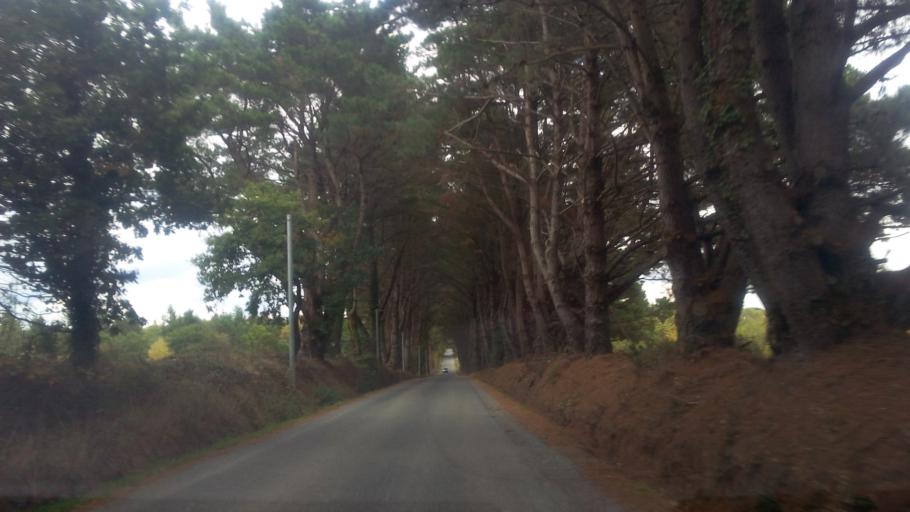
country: FR
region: Brittany
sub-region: Departement du Morbihan
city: Saint-Perreux
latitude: 47.6637
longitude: -2.1385
